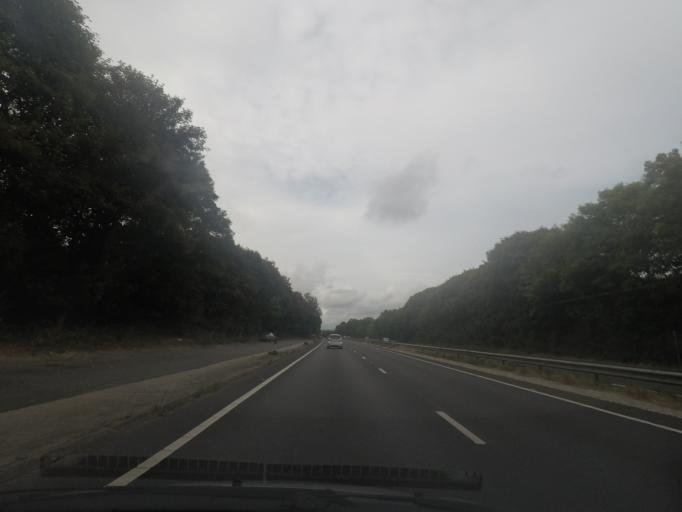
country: GB
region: England
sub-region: Hampshire
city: Overton
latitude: 51.2246
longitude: -1.3453
